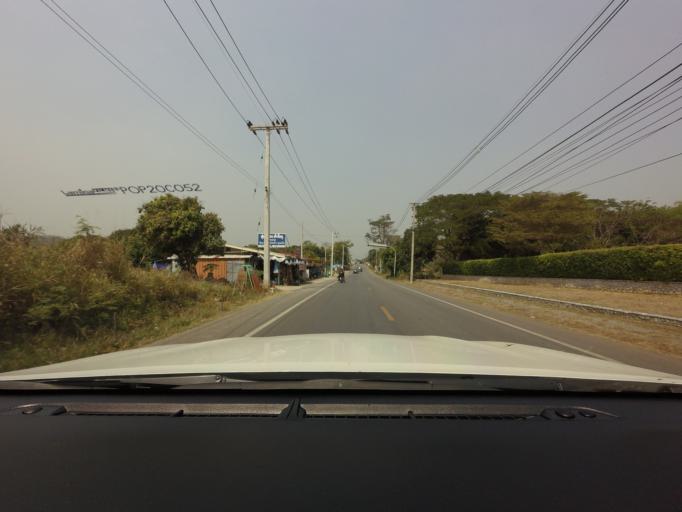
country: TH
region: Sara Buri
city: Muak Lek
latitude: 14.6063
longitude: 101.2130
